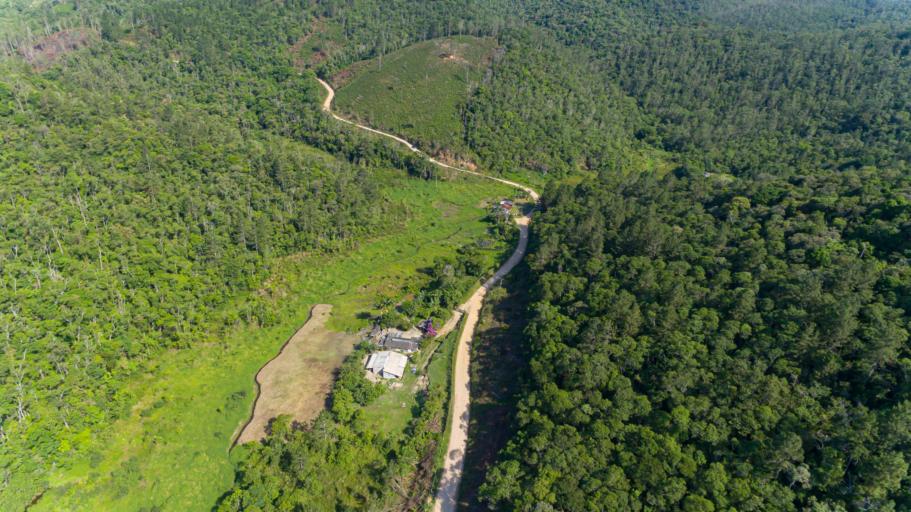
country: BR
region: Sao Paulo
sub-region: Juquitiba
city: Juquitiba
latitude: -24.0421
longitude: -47.2461
